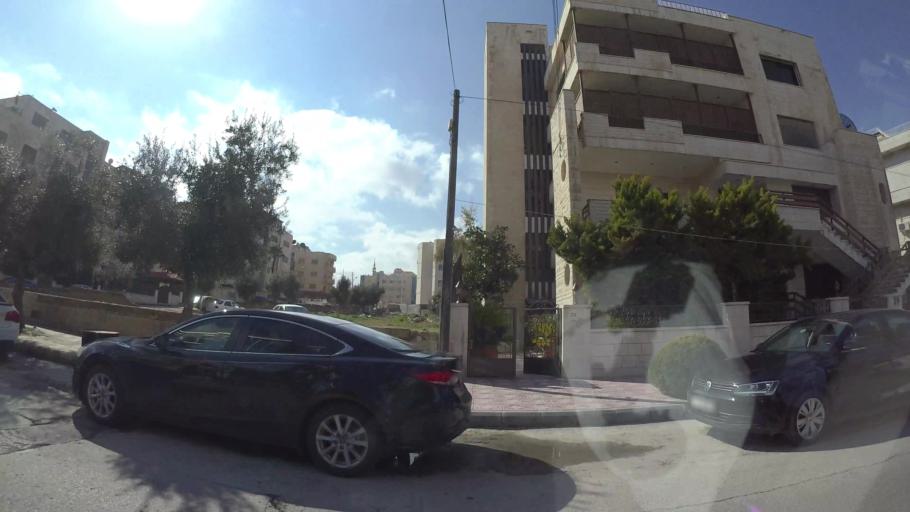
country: JO
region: Amman
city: Amman
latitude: 31.9749
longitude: 35.8963
